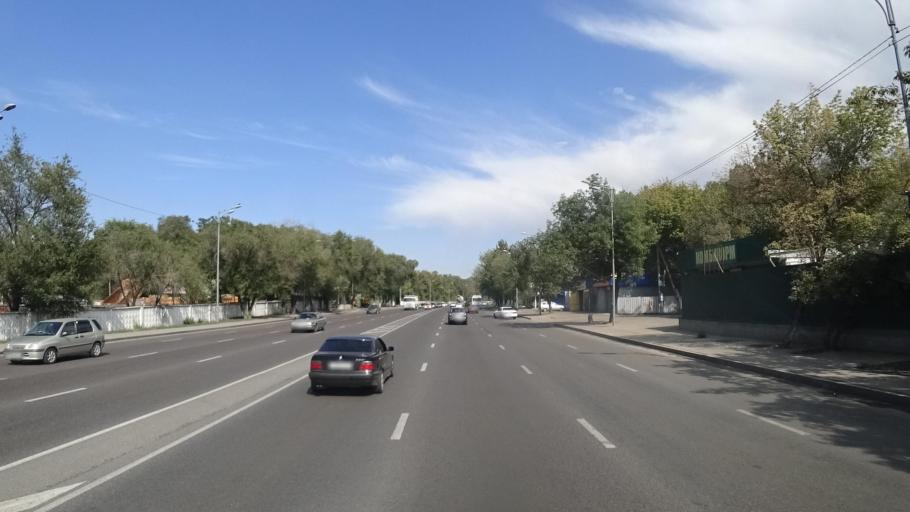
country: KZ
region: Almaty Qalasy
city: Almaty
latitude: 43.2771
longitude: 76.8987
